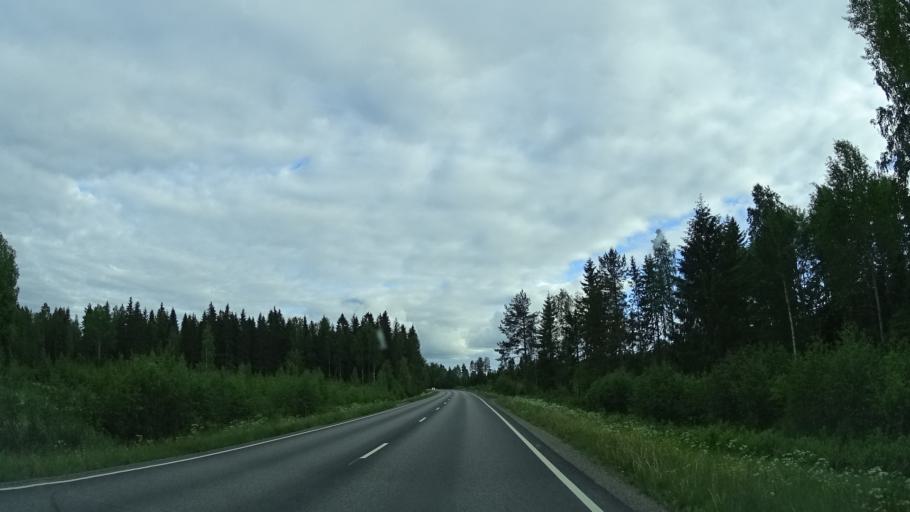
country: FI
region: Paijanne Tavastia
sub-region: Lahti
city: Sysmae
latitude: 61.4656
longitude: 25.7134
